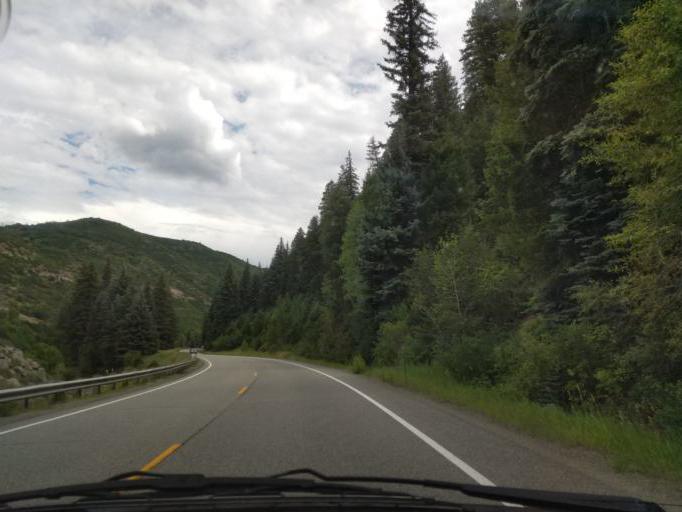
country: US
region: Colorado
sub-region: Delta County
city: Paonia
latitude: 38.9939
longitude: -107.3557
